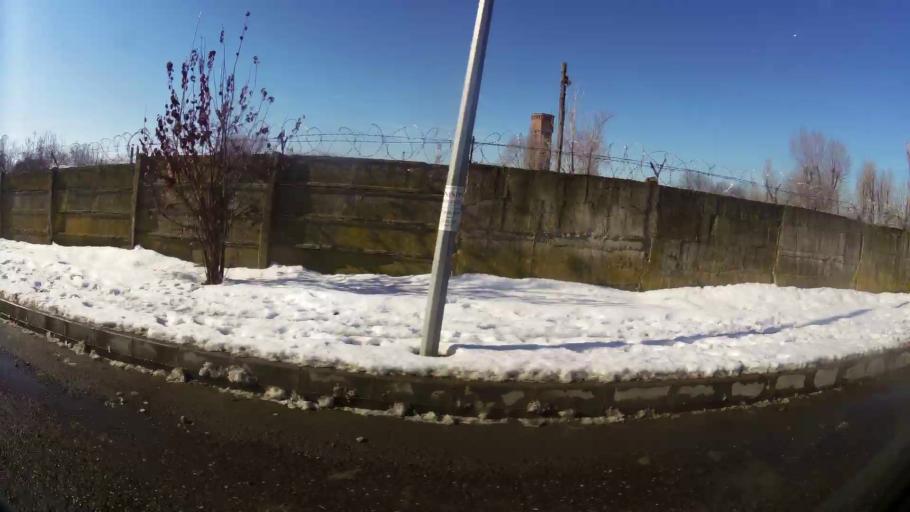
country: RO
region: Ilfov
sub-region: Comuna Magurele
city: Magurele
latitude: 44.3906
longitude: 26.0537
